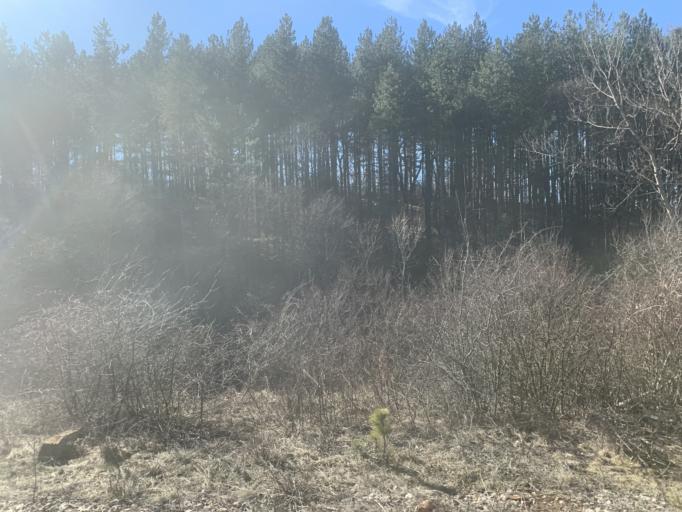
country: BG
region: Sofiya
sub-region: Obshtina Gorna Malina
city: Gorna Malina
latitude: 42.5633
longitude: 23.6887
